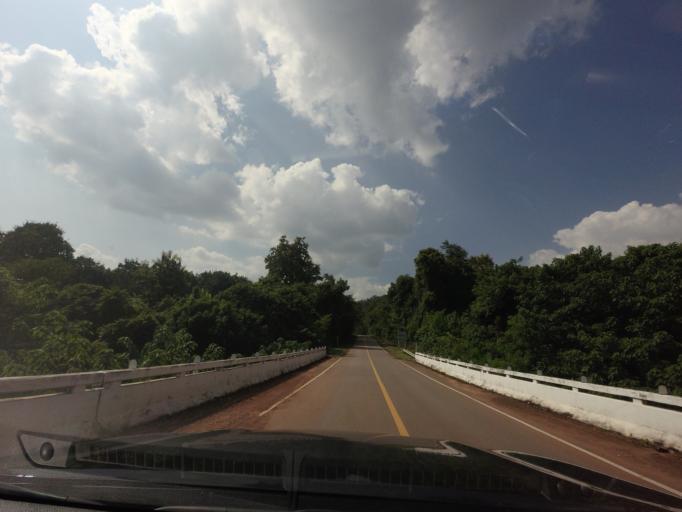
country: TH
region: Uttaradit
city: Ban Khok
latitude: 18.1841
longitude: 101.0658
